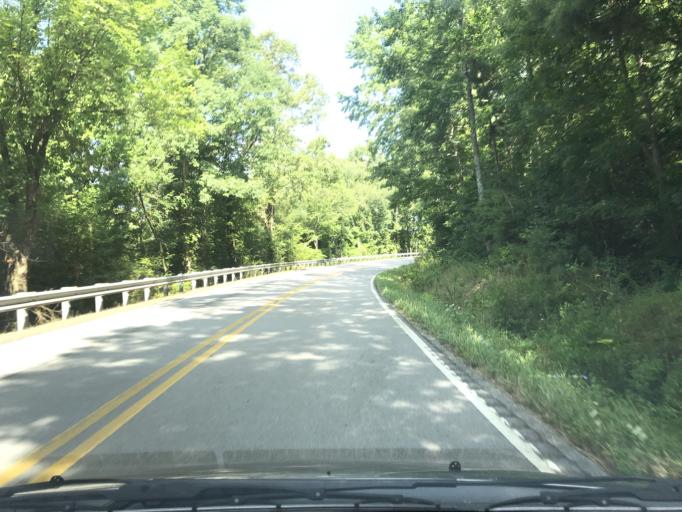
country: US
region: Tennessee
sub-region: Hamilton County
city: Lakesite
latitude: 35.2346
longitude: -85.0698
